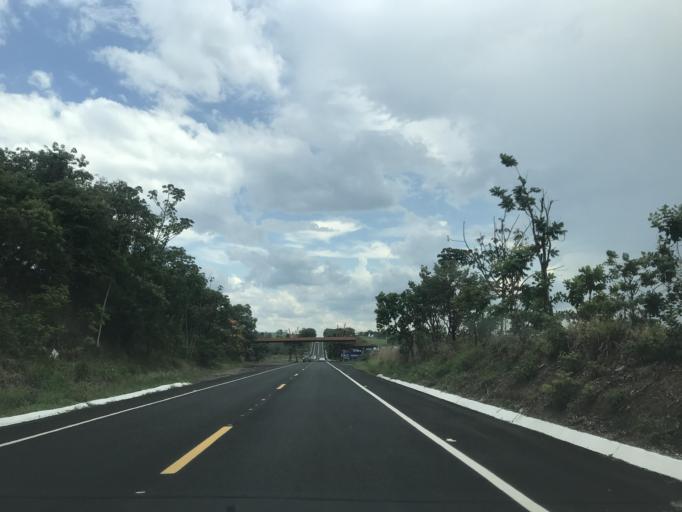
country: BR
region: Goias
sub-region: Caldas Novas
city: Caldas Novas
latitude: -17.7208
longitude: -48.7772
